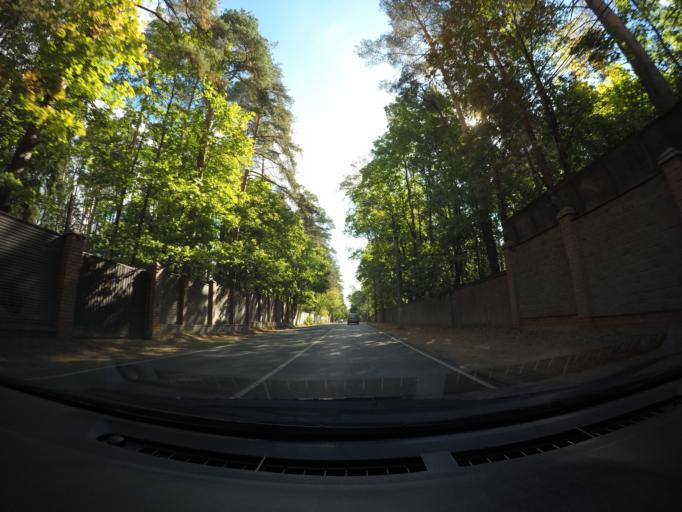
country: RU
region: Moskovskaya
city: Kratovo
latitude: 55.6034
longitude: 38.1570
